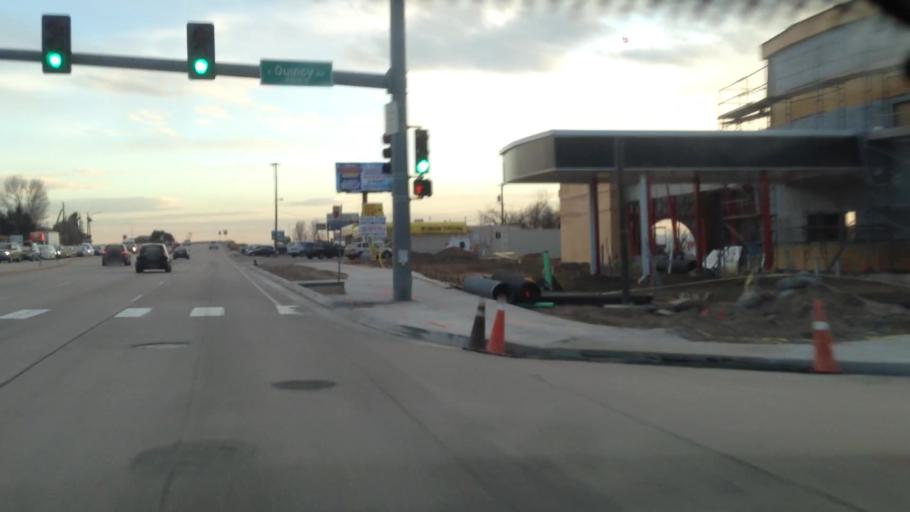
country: US
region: Colorado
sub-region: Arapahoe County
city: Dove Valley
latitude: 39.6386
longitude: -104.8291
